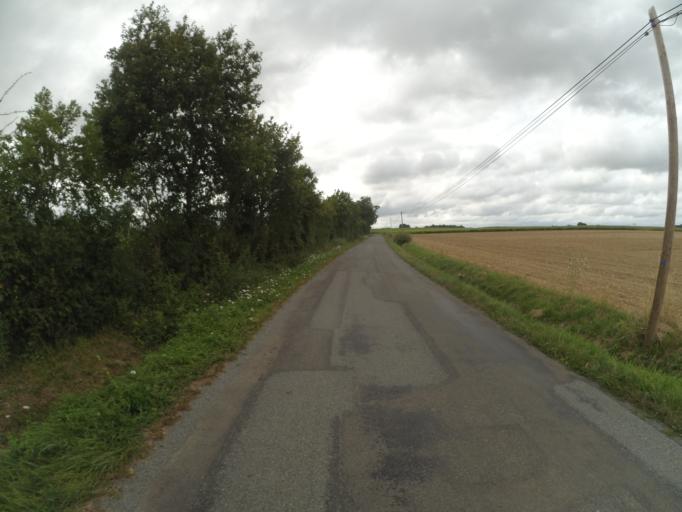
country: FR
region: Pays de la Loire
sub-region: Departement de la Vendee
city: Saint-Philbert-de-Bouaine
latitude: 47.0065
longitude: -1.5340
